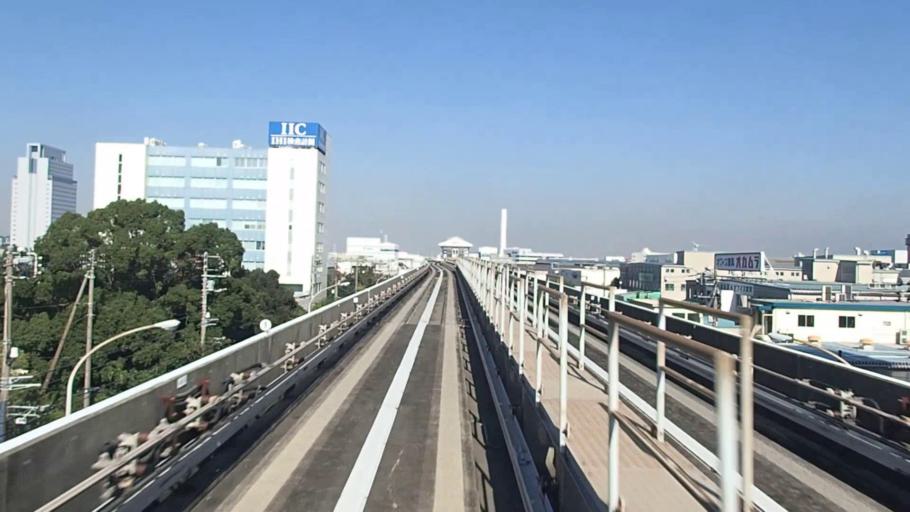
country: JP
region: Kanagawa
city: Yokosuka
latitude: 35.3480
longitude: 139.6486
